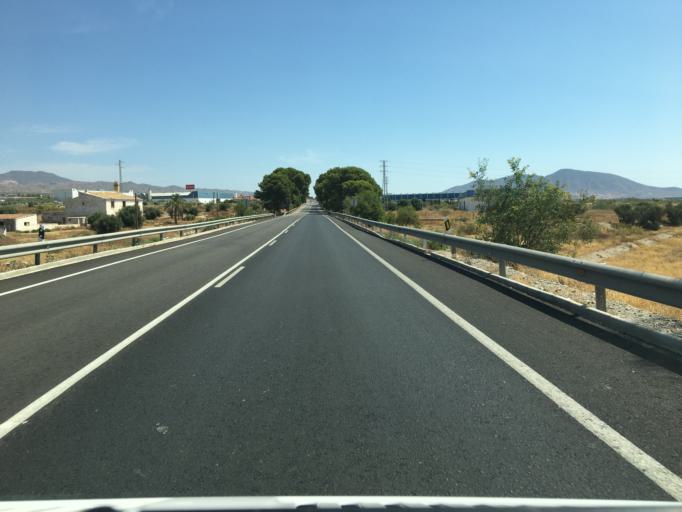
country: ES
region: Andalusia
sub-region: Provincia de Almeria
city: Huercal-Overa
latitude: 37.4288
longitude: -1.9142
